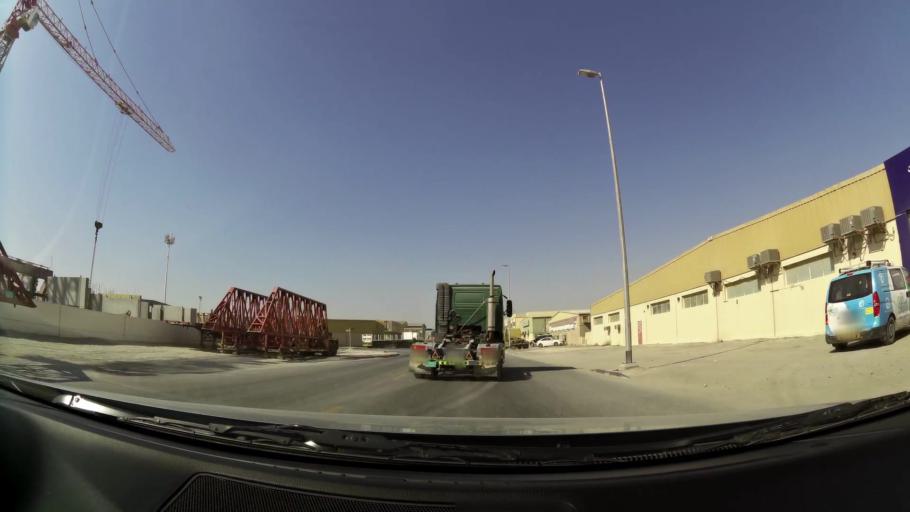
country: AE
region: Dubai
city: Dubai
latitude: 25.1216
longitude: 55.2200
